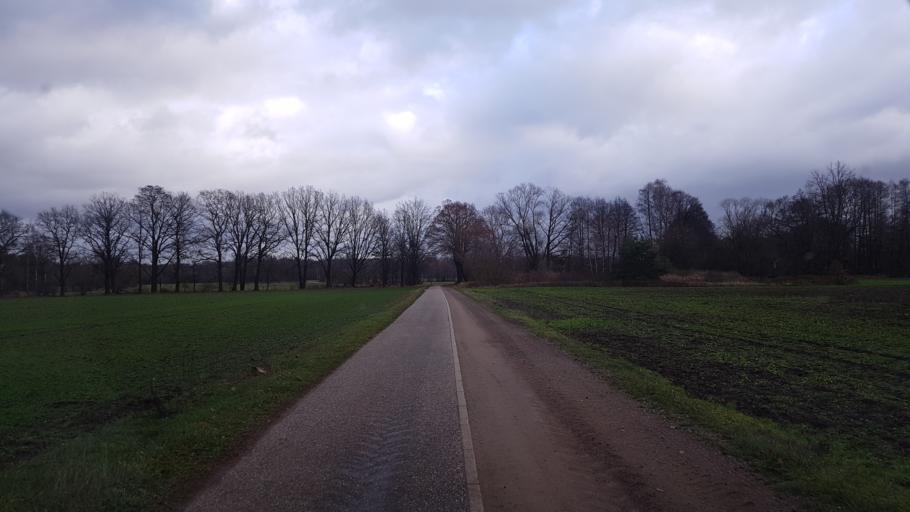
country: DE
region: Brandenburg
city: Finsterwalde
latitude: 51.5975
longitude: 13.6412
